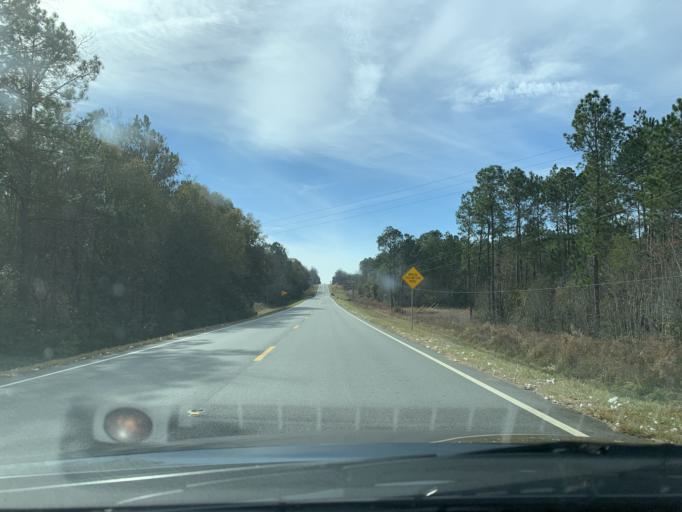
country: US
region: Georgia
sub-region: Turner County
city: Ashburn
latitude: 31.7544
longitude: -83.5535
